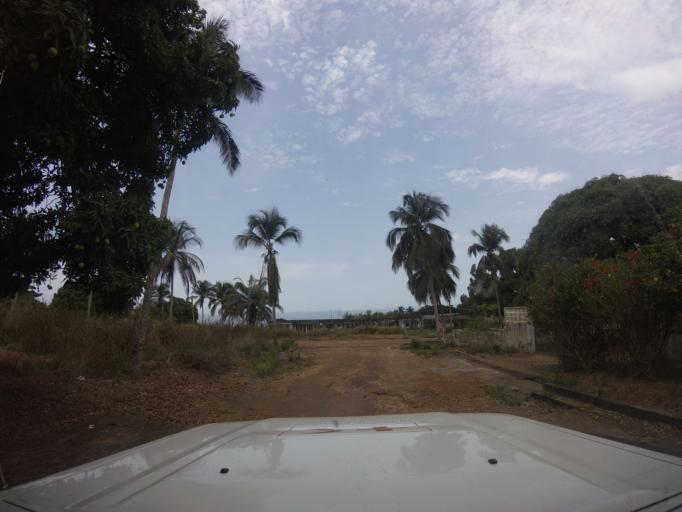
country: LR
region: Grand Cape Mount
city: Robertsport
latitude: 6.7508
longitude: -11.3789
